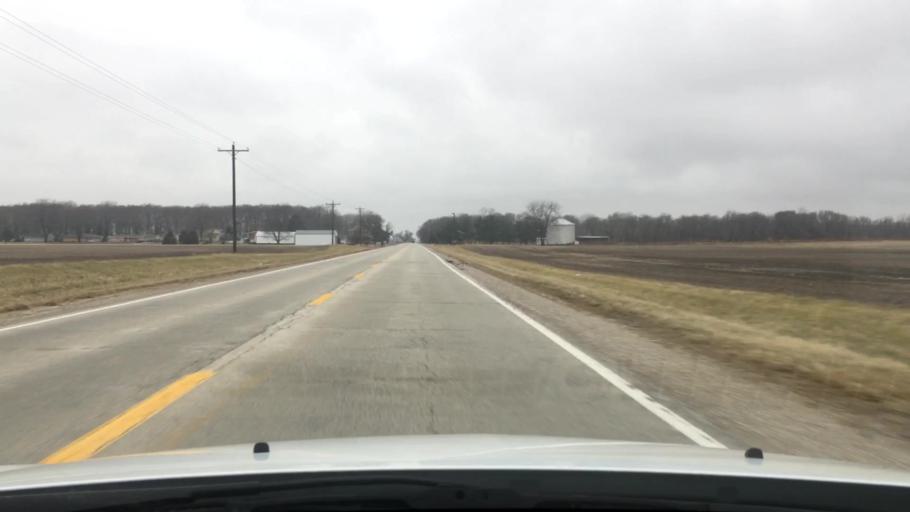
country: US
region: Illinois
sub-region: Iroquois County
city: Clifton
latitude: 40.8880
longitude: -87.8247
